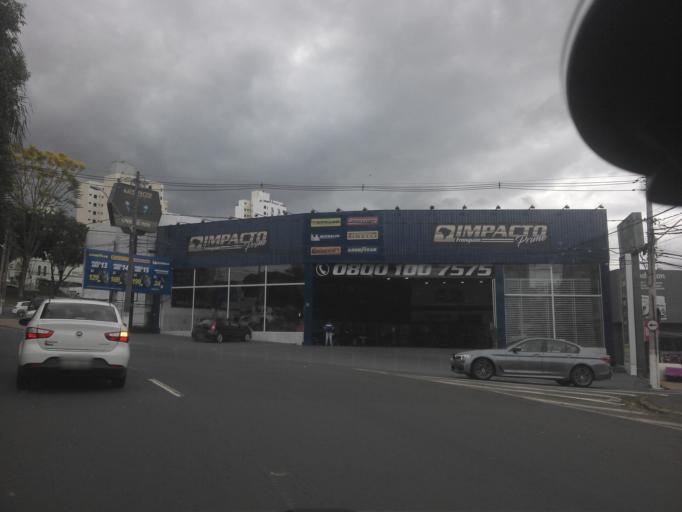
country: BR
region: Sao Paulo
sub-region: Campinas
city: Campinas
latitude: -22.8818
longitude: -47.0644
